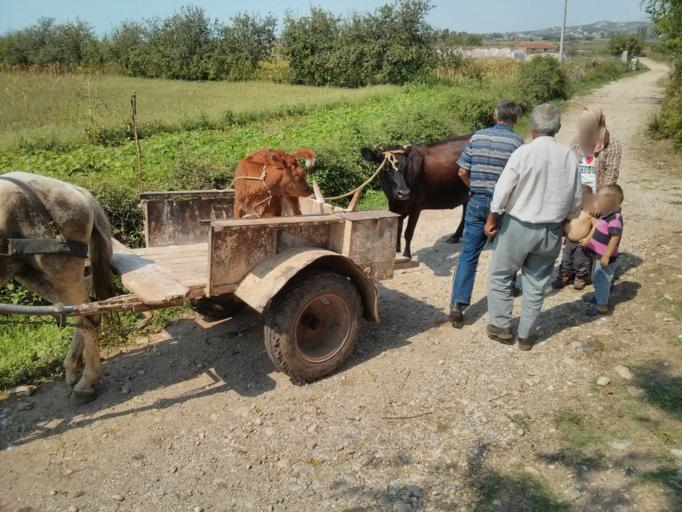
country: AL
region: Shkoder
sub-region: Rrethi i Malesia e Madhe
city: Gruemire
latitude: 42.1389
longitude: 19.5450
